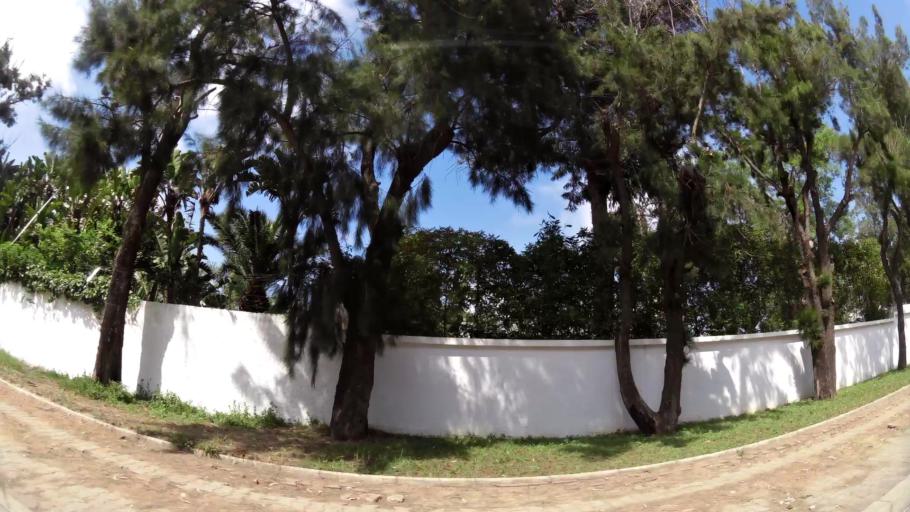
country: MA
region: Rabat-Sale-Zemmour-Zaer
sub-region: Rabat
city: Rabat
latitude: 33.9793
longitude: -6.8419
